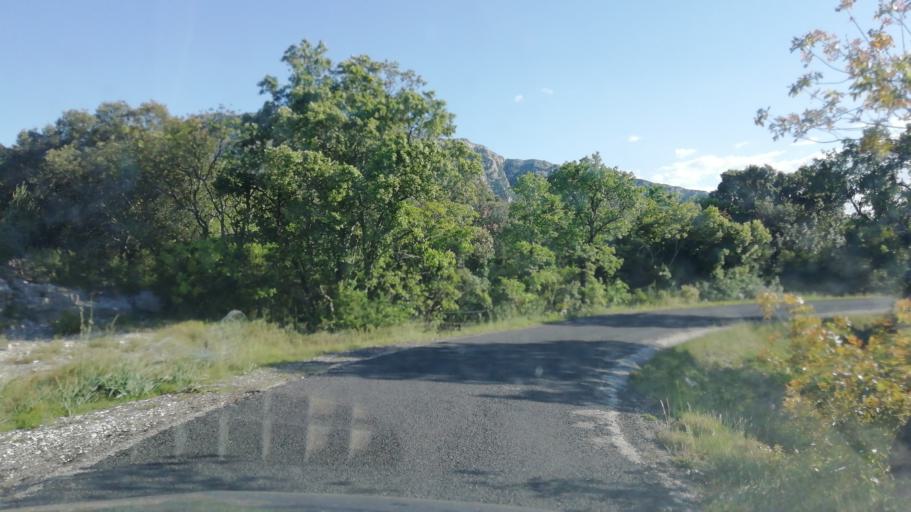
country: FR
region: Languedoc-Roussillon
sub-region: Departement de l'Herault
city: Saint-Mathieu-de-Treviers
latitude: 43.7945
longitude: 3.8107
